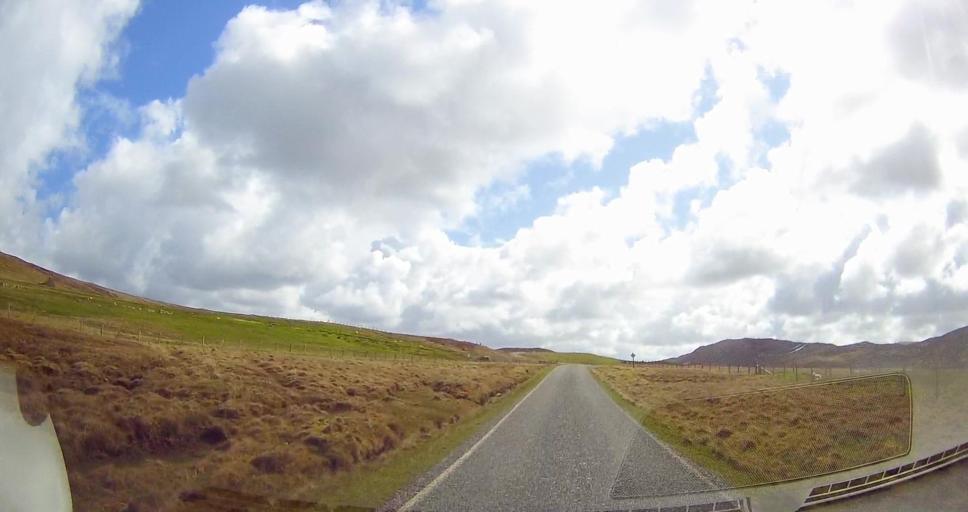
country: GB
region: Scotland
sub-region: Shetland Islands
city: Lerwick
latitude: 60.5655
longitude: -1.3335
